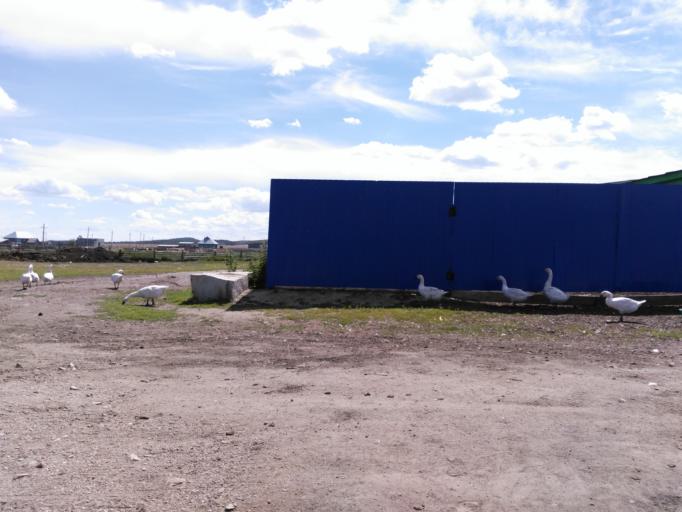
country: RU
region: Bashkortostan
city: Akhunovo
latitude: 54.2015
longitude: 59.5951
